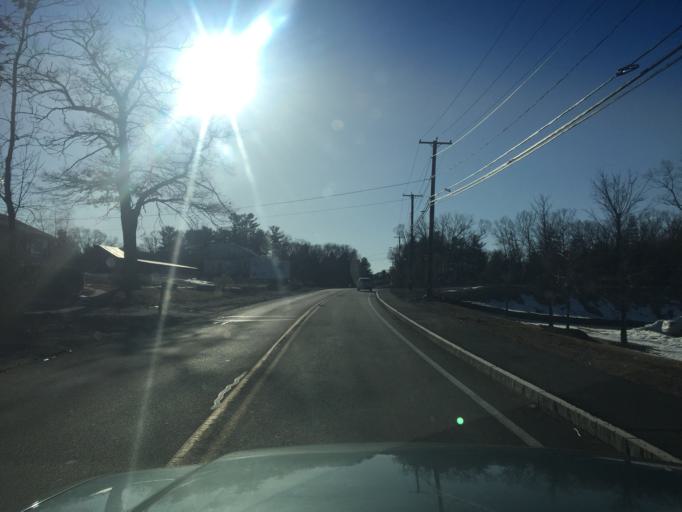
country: US
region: Massachusetts
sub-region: Norfolk County
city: Bellingham
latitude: 42.0824
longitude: -71.4588
